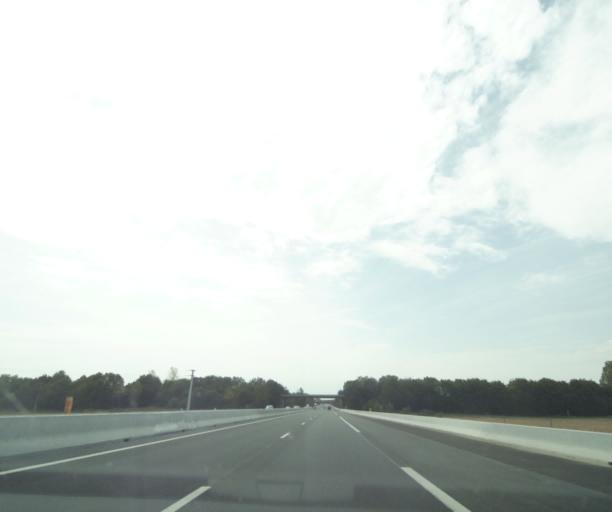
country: FR
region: Poitou-Charentes
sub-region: Departement des Deux-Sevres
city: Beauvoir-sur-Niort
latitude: 46.2085
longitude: -0.4646
